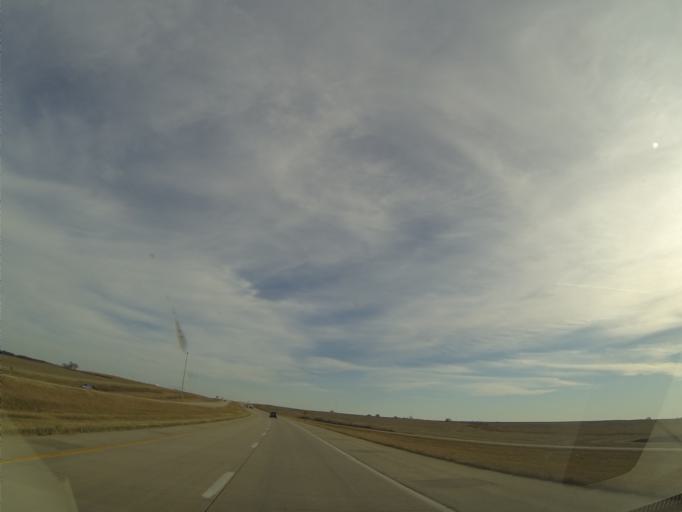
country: US
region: Kansas
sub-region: Ottawa County
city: Minneapolis
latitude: 39.1155
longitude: -97.6654
